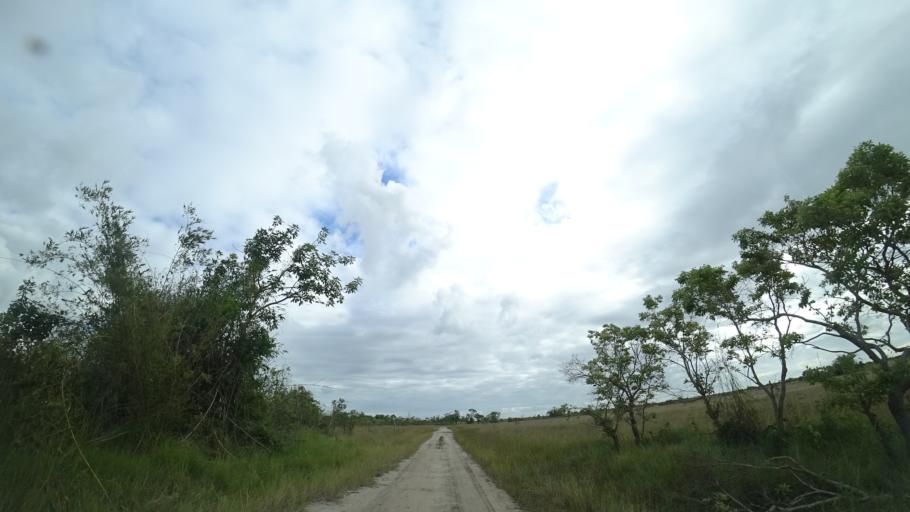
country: MZ
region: Sofala
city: Beira
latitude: -19.6158
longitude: 35.0632
